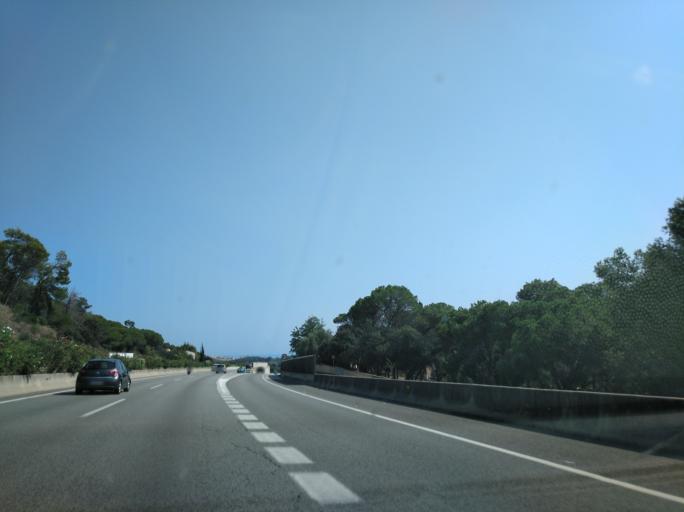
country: ES
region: Catalonia
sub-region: Provincia de Barcelona
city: Argentona
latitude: 41.5774
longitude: 2.3832
